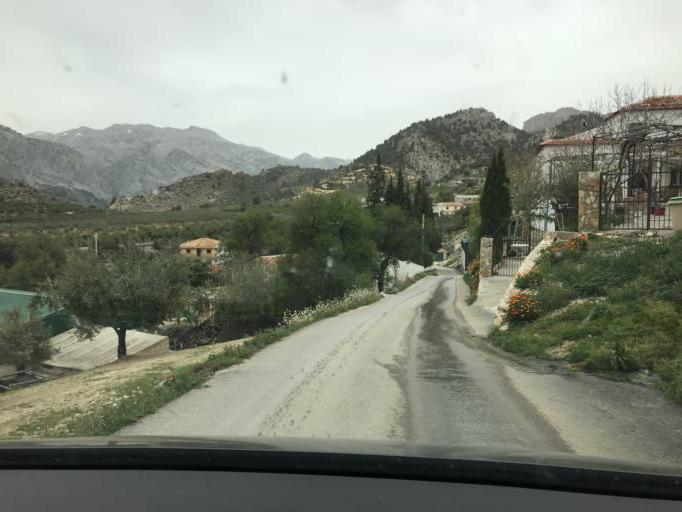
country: ES
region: Andalusia
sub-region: Provincia de Granada
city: Castril
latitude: 37.8176
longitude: -2.7675
